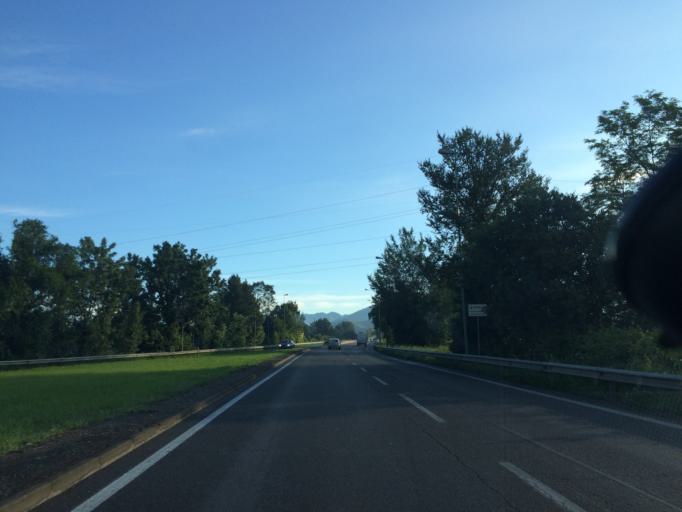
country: IT
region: Lombardy
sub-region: Provincia di Brescia
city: Roncadelle
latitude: 45.5088
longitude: 10.1671
